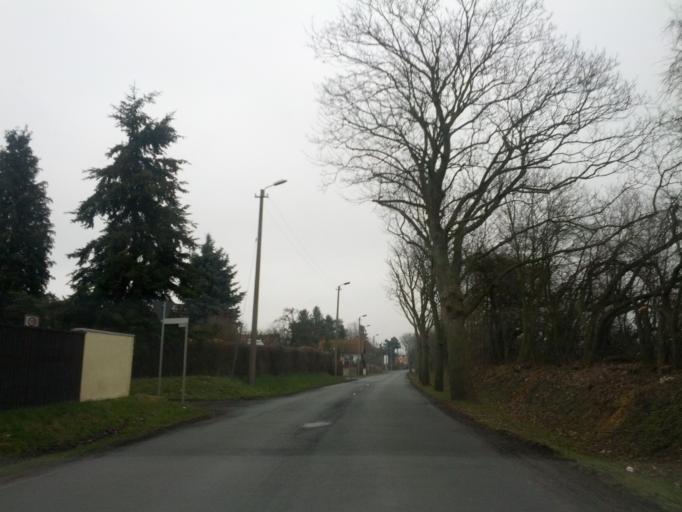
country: DE
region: Thuringia
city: Gotha
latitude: 50.9627
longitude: 10.6880
